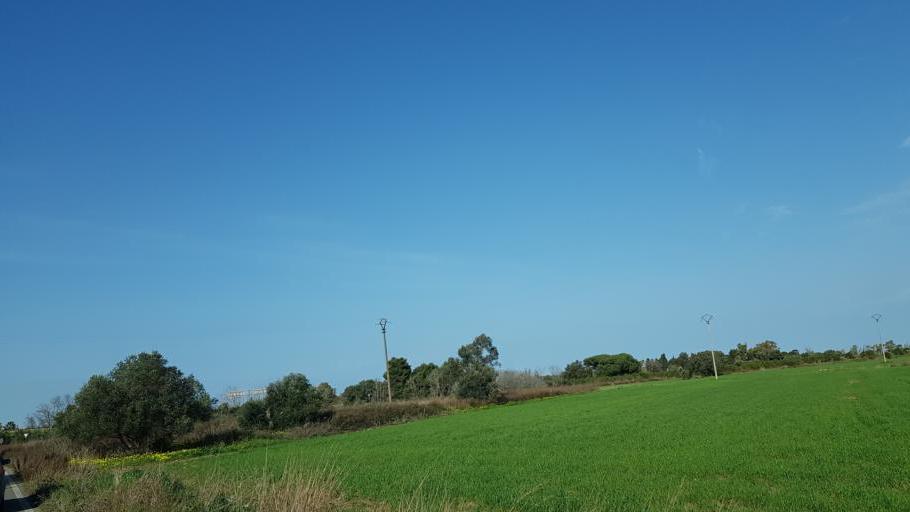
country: IT
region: Apulia
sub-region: Provincia di Brindisi
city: Brindisi
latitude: 40.6532
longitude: 17.9062
